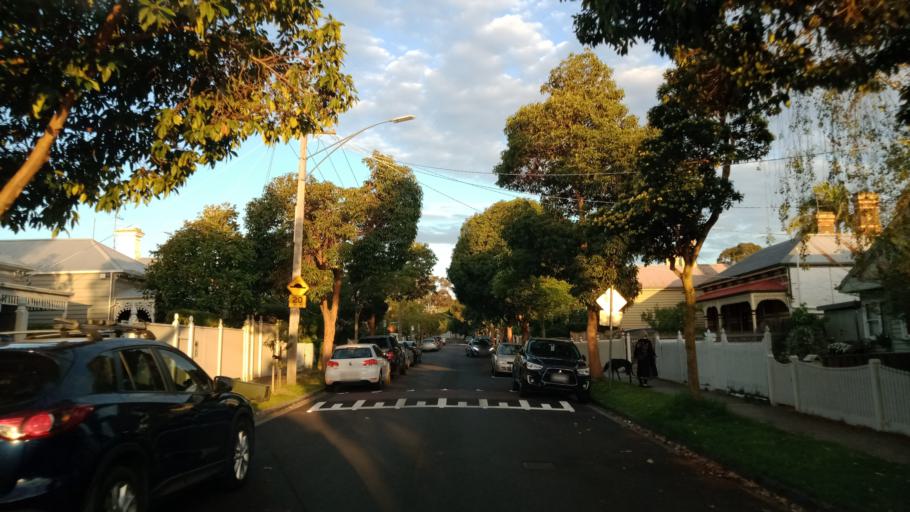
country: AU
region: Victoria
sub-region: Boroondara
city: Hawthorn East
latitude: -37.8267
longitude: 145.0493
